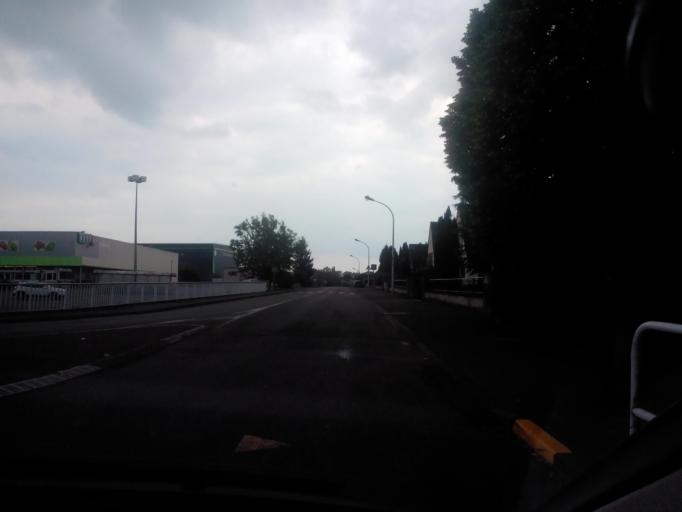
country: FR
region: Alsace
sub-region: Departement du Bas-Rhin
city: Sarre-Union
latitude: 48.9345
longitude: 7.0896
